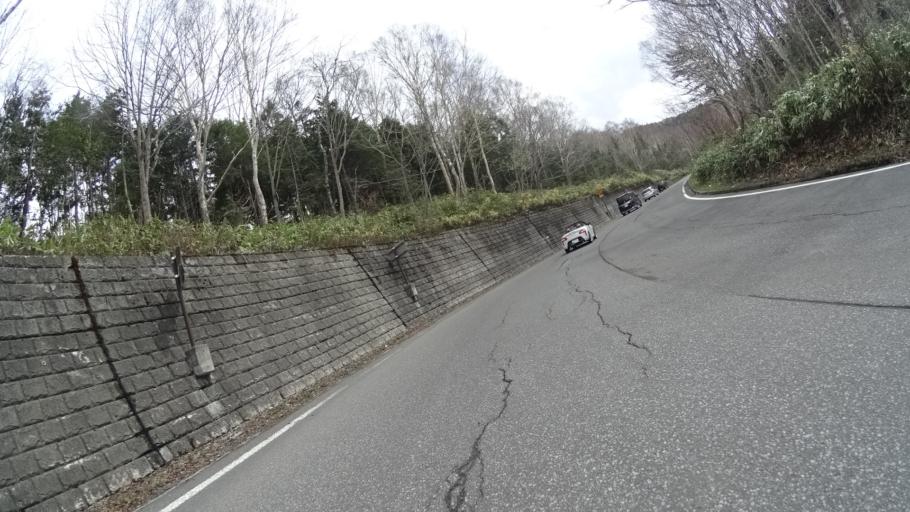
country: JP
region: Nagano
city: Nakano
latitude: 36.7137
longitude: 138.4959
